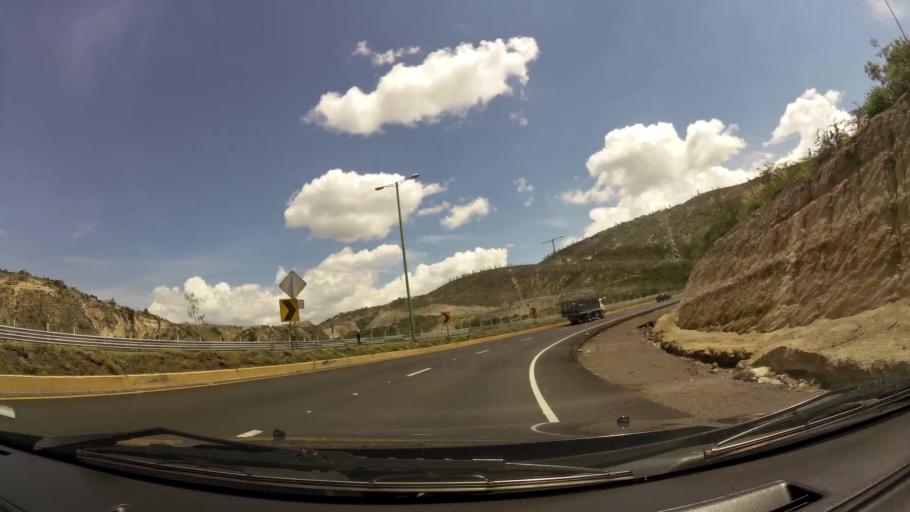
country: EC
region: Pichincha
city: Quito
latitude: -0.0897
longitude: -78.3958
